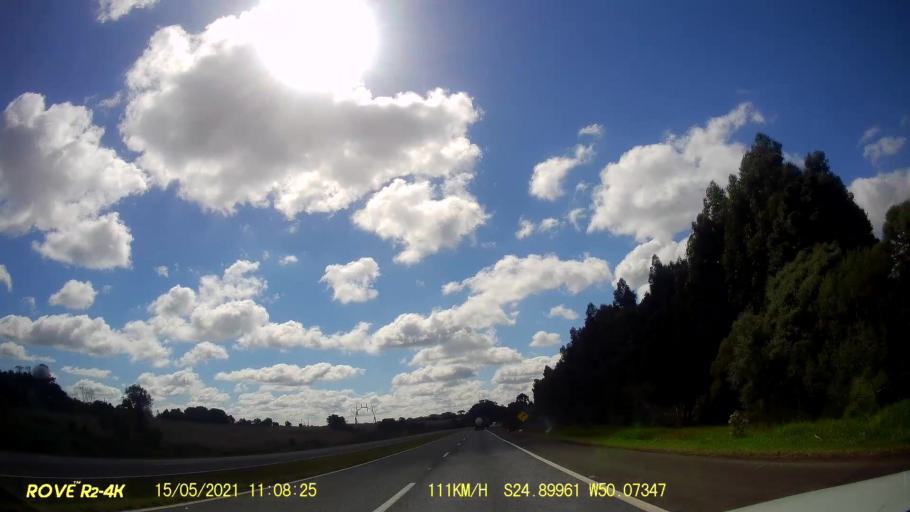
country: BR
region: Parana
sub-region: Carambei
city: Carambei
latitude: -24.8999
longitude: -50.0735
